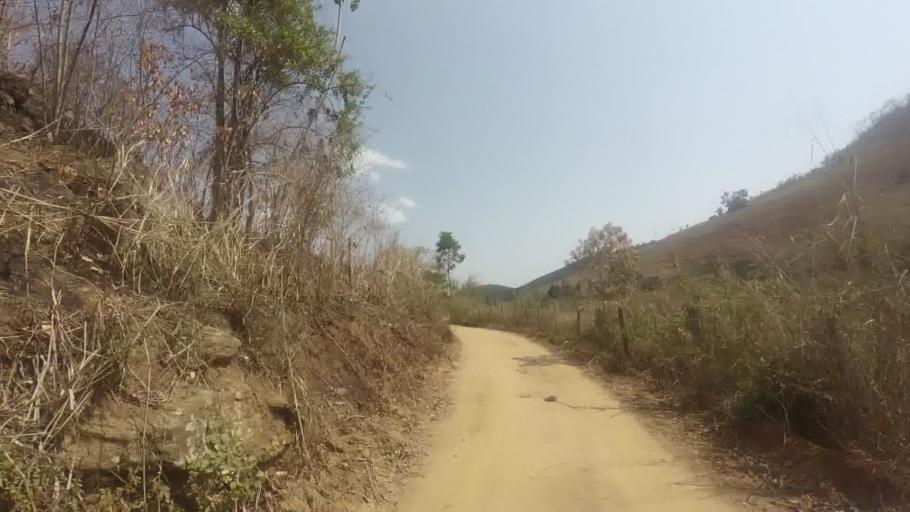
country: BR
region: Espirito Santo
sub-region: Sao Jose Do Calcado
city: Sao Jose do Calcado
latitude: -21.0147
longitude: -41.5144
